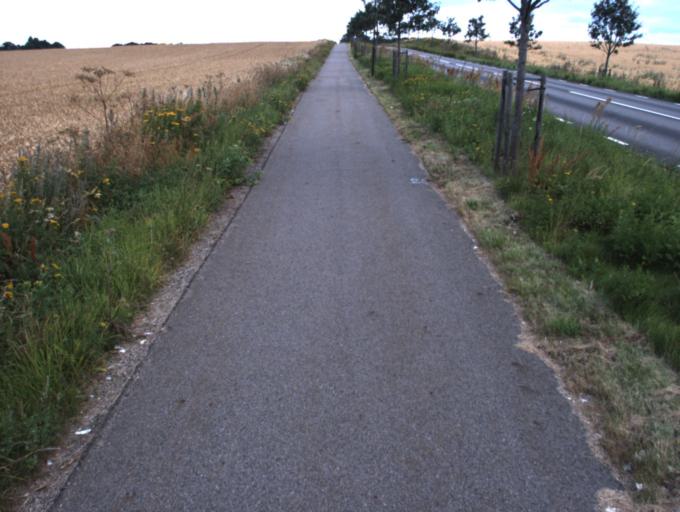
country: DK
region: Capital Region
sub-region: Helsingor Kommune
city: Helsingor
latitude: 56.1023
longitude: 12.6451
